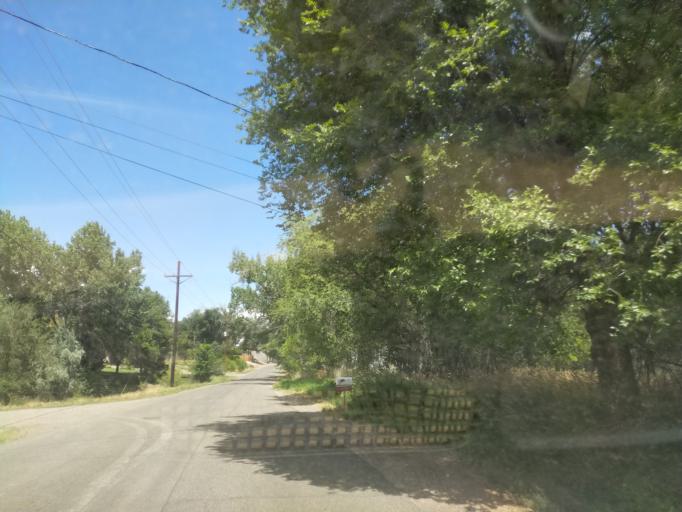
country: US
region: Colorado
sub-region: Mesa County
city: Redlands
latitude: 39.0769
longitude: -108.6378
